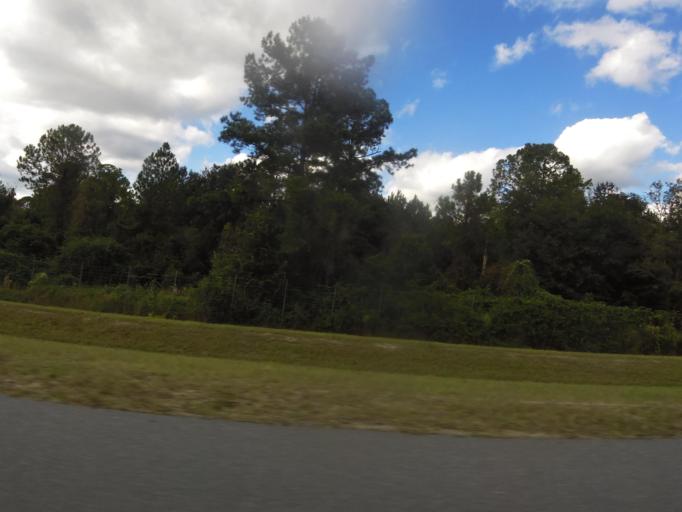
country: US
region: Florida
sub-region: Bradford County
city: Starke
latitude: 29.9822
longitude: -82.1150
